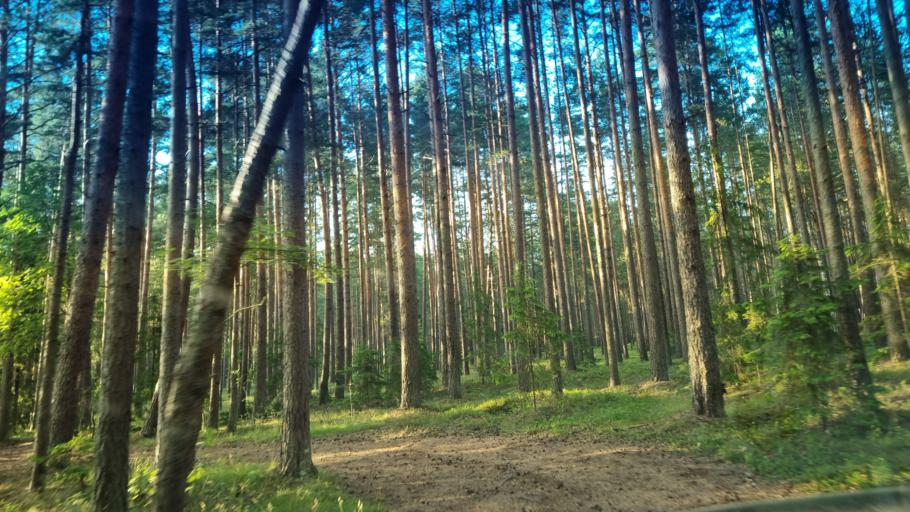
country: LV
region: Kuldigas Rajons
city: Kuldiga
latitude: 57.1918
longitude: 22.1834
